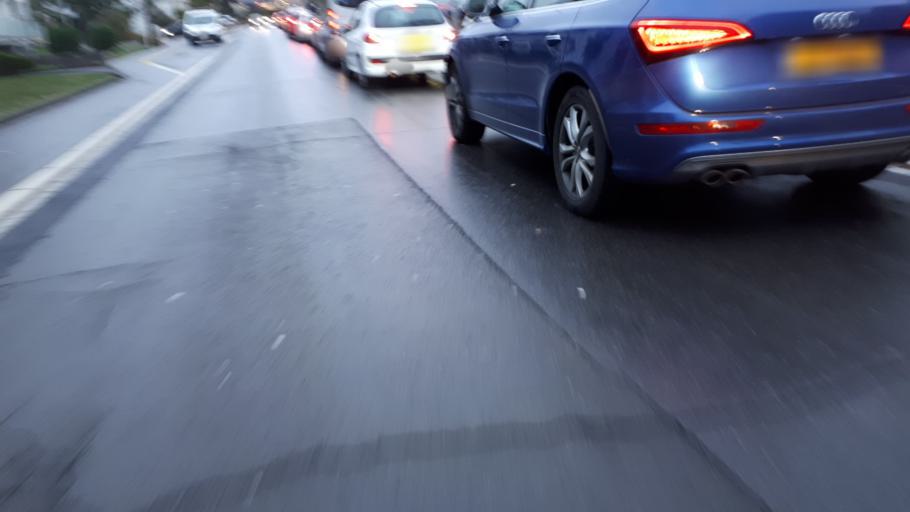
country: LU
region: Luxembourg
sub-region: Canton de Luxembourg
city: Strassen
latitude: 49.6193
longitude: 6.0649
